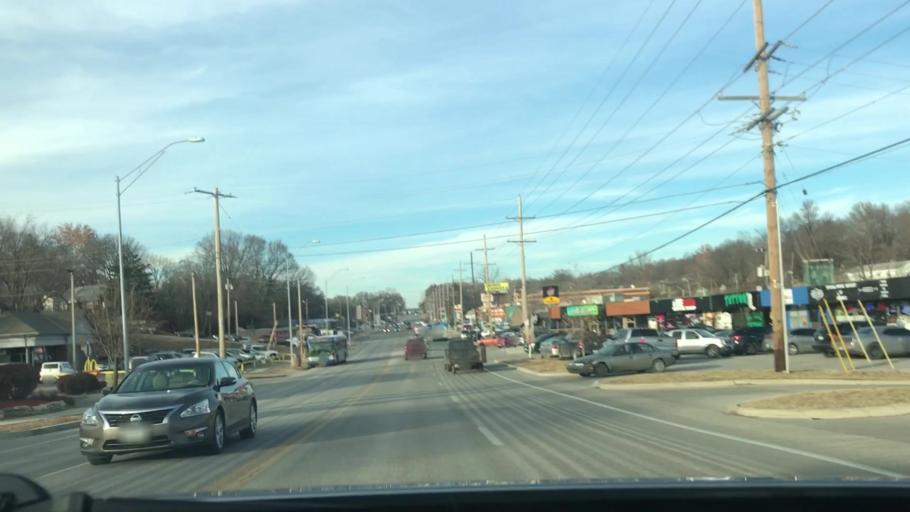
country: US
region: Missouri
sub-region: Platte County
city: Riverside
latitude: 39.1671
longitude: -94.5768
